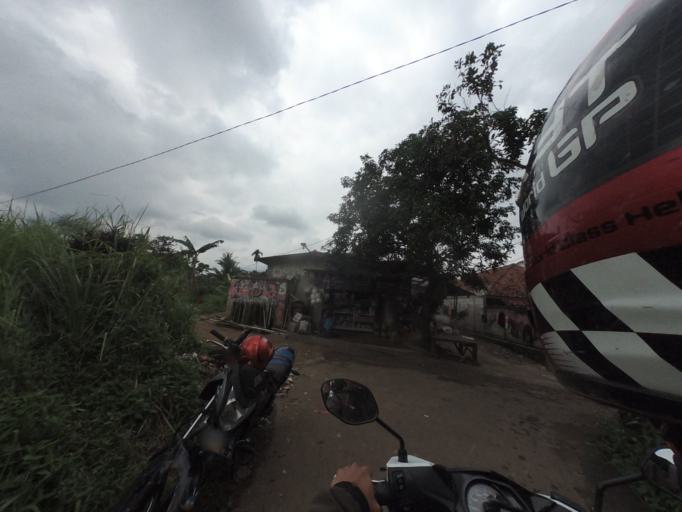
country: ID
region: West Java
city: Bogor
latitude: -6.6157
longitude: 106.7364
